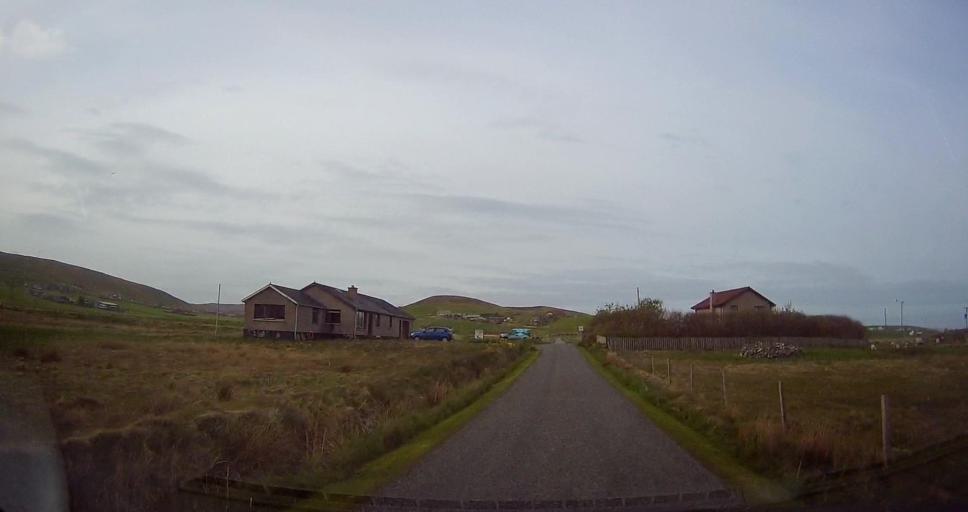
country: GB
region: Scotland
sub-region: Shetland Islands
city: Sandwick
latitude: 60.0431
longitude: -1.2171
